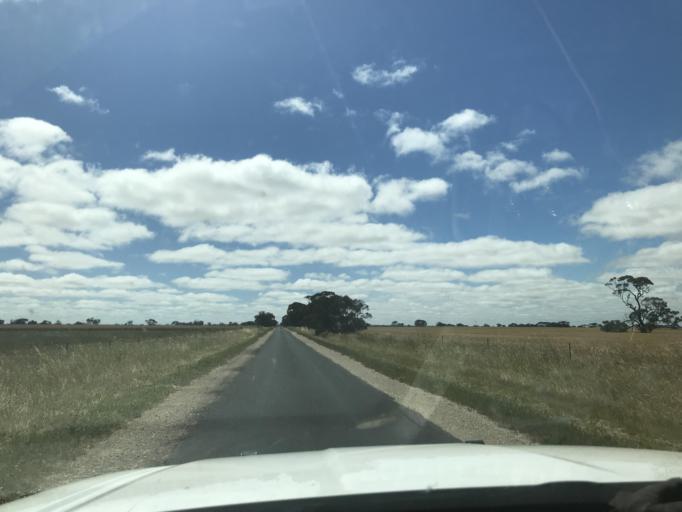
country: AU
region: South Australia
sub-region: Tatiara
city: Bordertown
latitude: -36.2808
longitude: 141.1383
